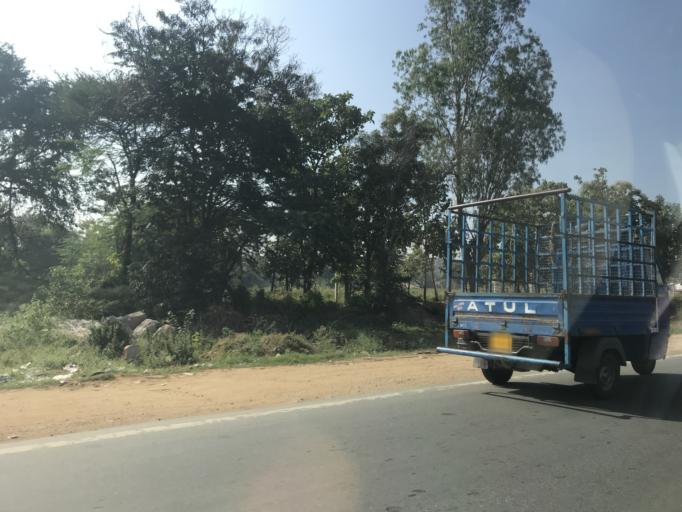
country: IN
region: Karnataka
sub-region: Mandya
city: Maddur
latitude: 12.5749
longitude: 77.0168
